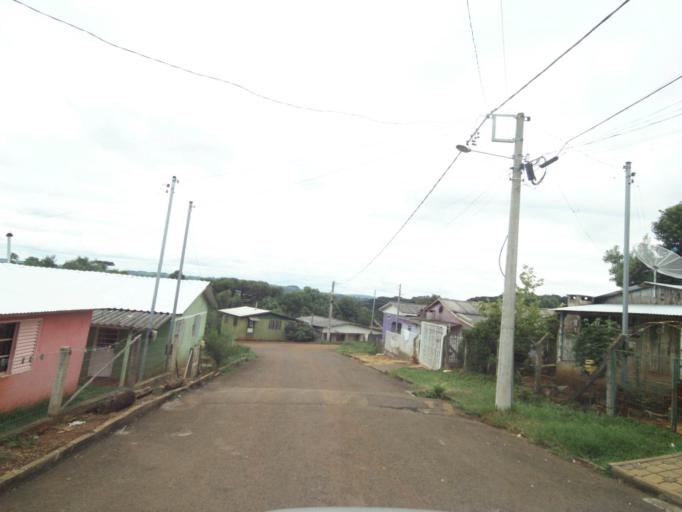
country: BR
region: Rio Grande do Sul
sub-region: Lagoa Vermelha
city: Lagoa Vermelha
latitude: -28.2149
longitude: -51.5389
